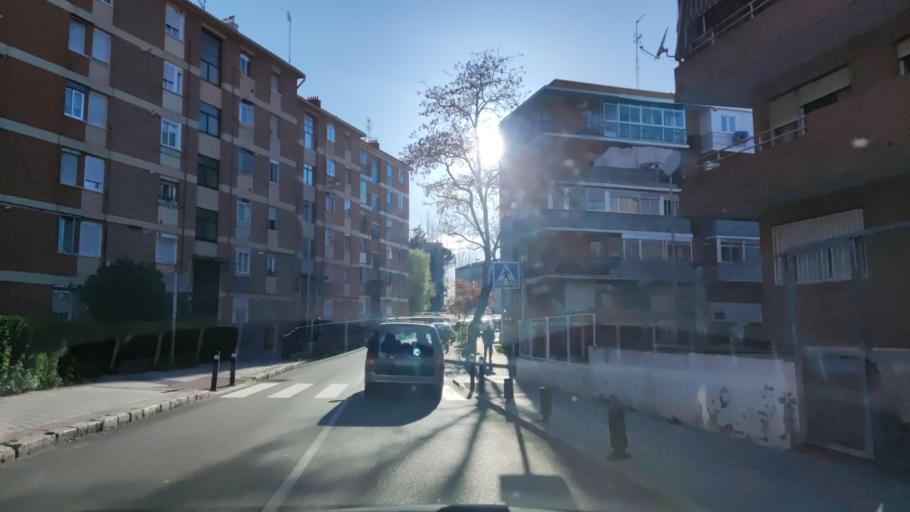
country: ES
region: Madrid
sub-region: Provincia de Madrid
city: Latina
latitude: 40.3966
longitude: -3.7725
